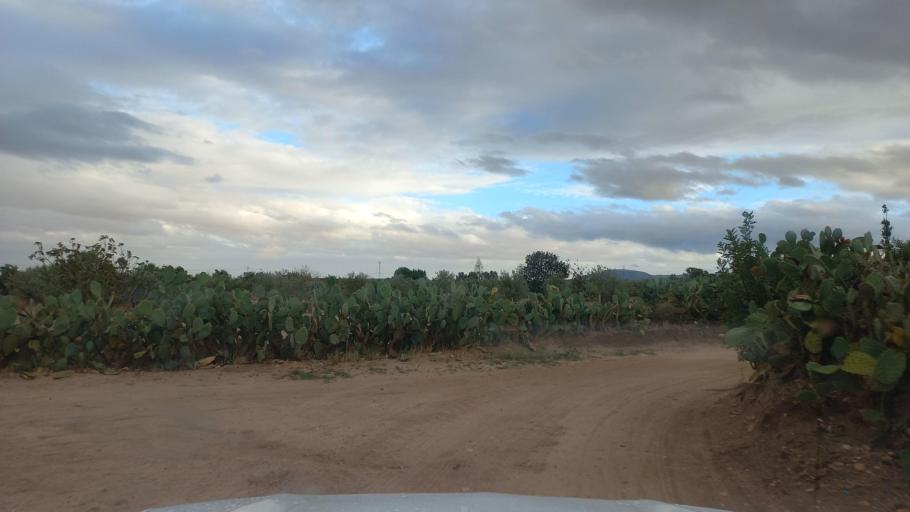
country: TN
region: Al Qasrayn
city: Kasserine
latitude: 35.2617
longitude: 8.9355
